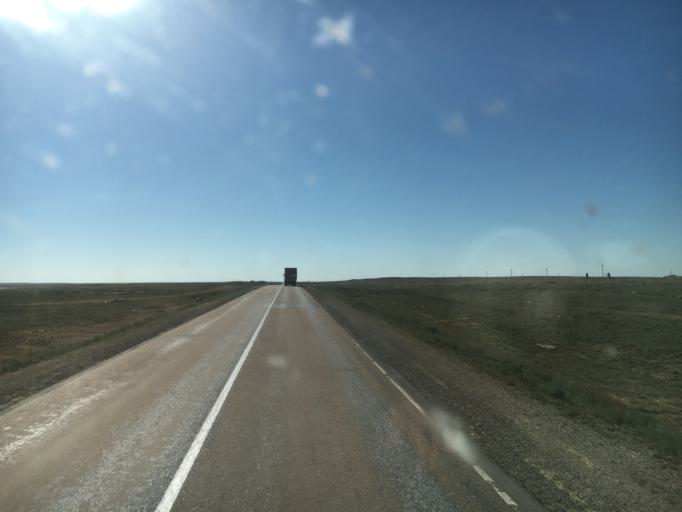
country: RU
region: Orenburg
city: Dombarovskiy
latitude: 50.0814
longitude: 59.5709
